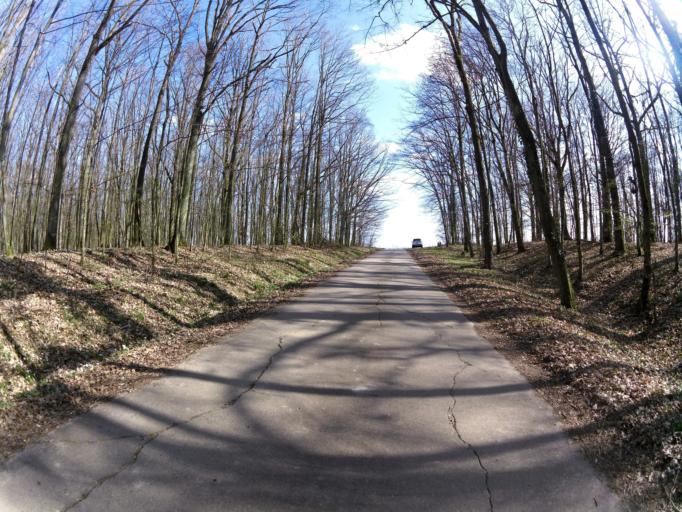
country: DE
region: Bavaria
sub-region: Regierungsbezirk Unterfranken
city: Nordheim
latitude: 49.8412
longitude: 10.1638
